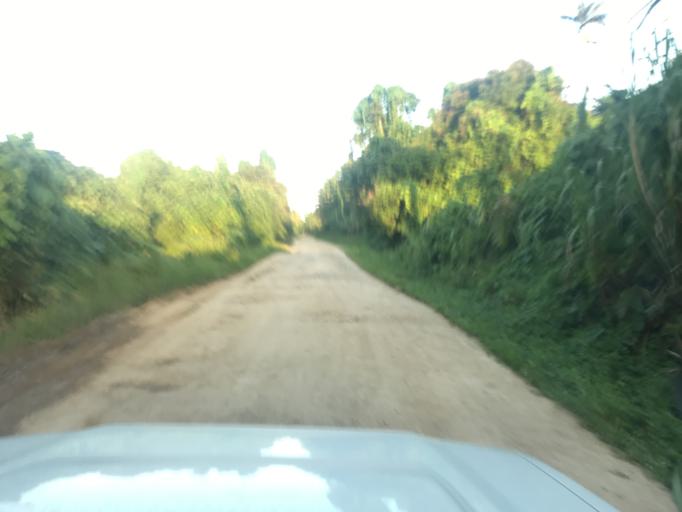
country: VU
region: Sanma
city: Luganville
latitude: -15.5703
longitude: 166.9522
